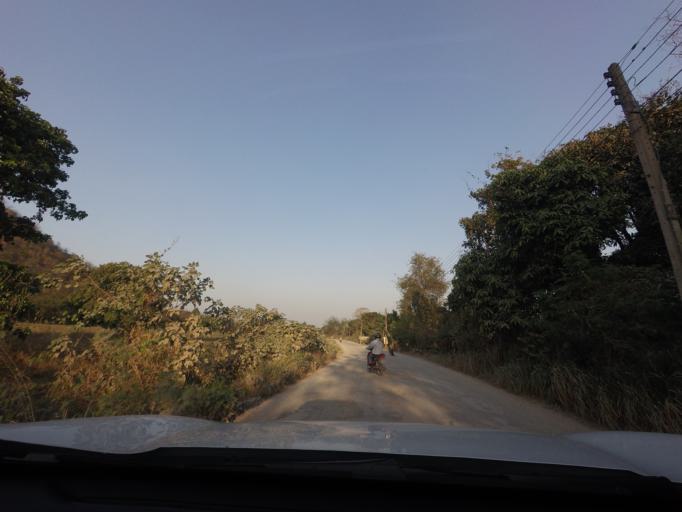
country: TH
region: Nakhon Ratchasima
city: Pak Chong
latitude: 14.6405
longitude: 101.3680
